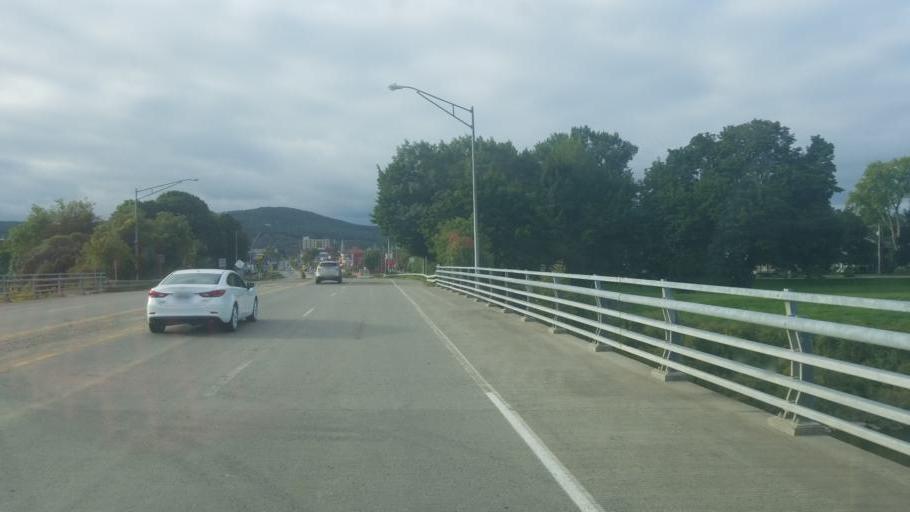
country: US
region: New York
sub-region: Cattaraugus County
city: Olean
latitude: 42.0887
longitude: -78.4299
